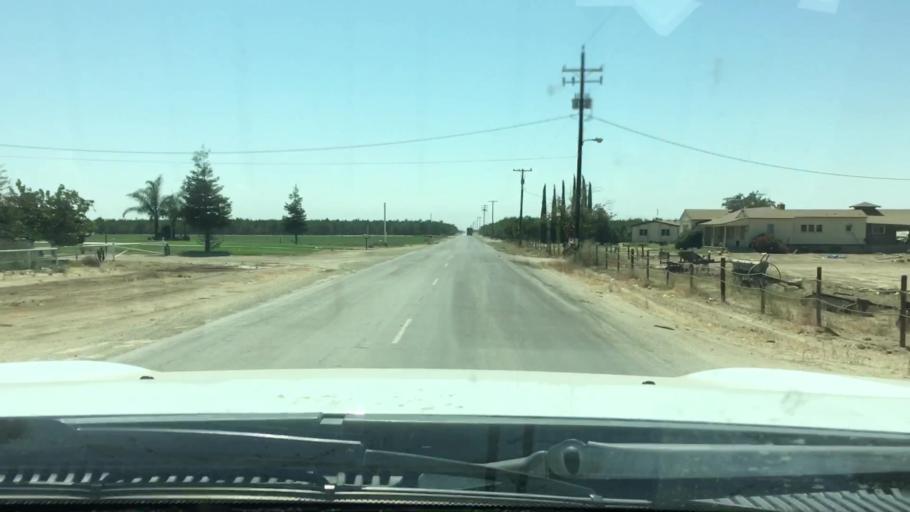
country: US
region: California
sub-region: Kern County
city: Wasco
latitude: 35.5431
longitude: -119.4031
